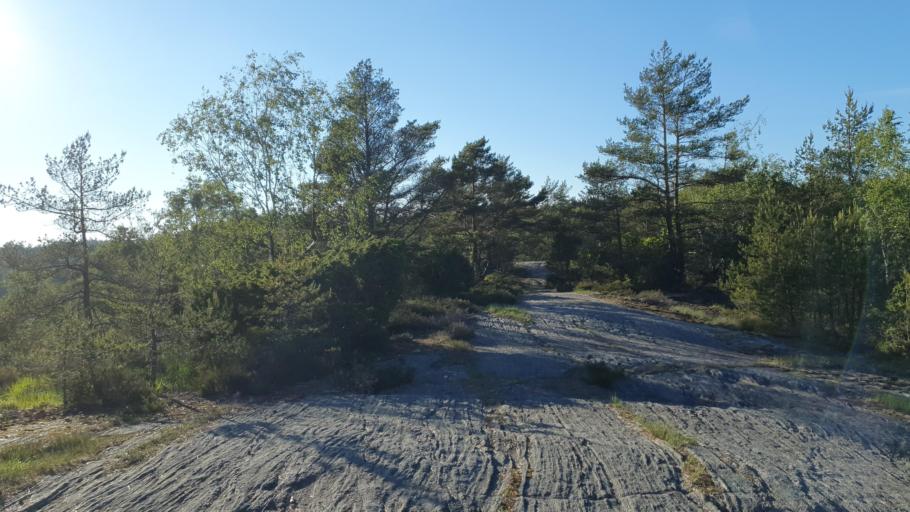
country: SE
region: Vaestra Goetaland
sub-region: Molndal
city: Kallered
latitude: 57.6304
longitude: 12.0623
